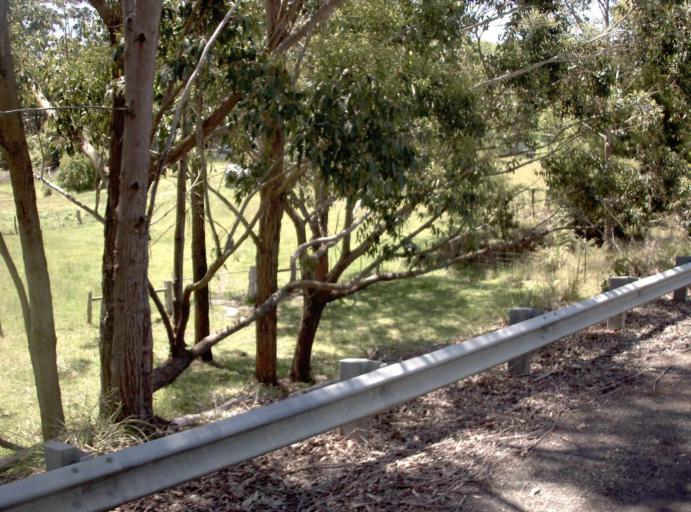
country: AU
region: Victoria
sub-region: East Gippsland
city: Lakes Entrance
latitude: -37.7009
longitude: 148.7167
